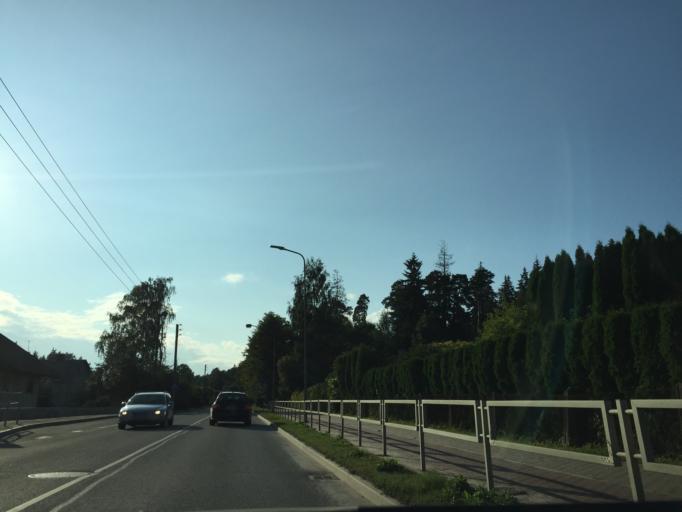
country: LV
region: Ogre
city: Ogre
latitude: 56.8153
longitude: 24.6258
